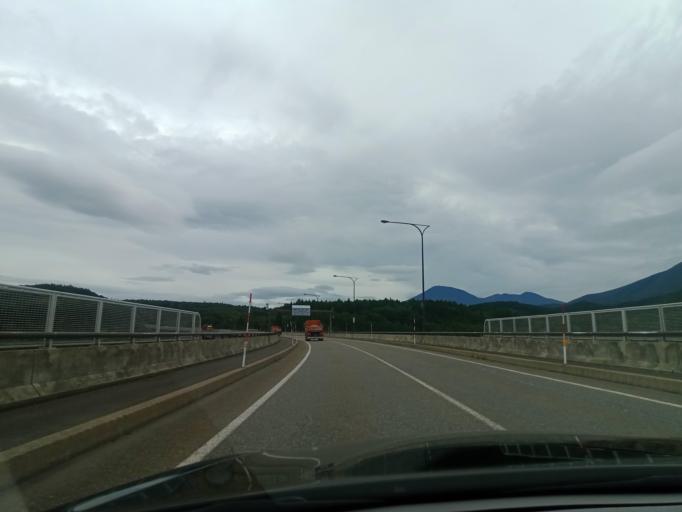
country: JP
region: Niigata
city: Arai
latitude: 36.8553
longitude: 138.1926
